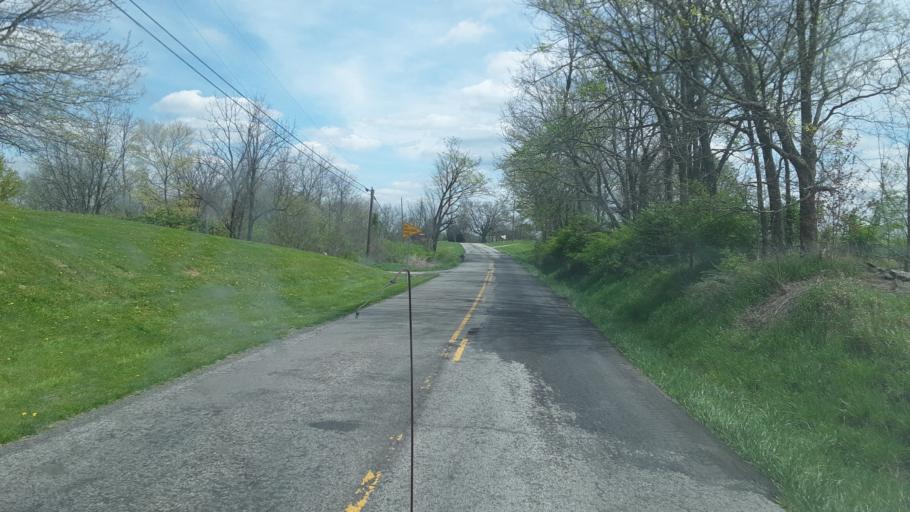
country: US
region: Kentucky
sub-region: Owen County
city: Owenton
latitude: 38.6410
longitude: -84.7650
